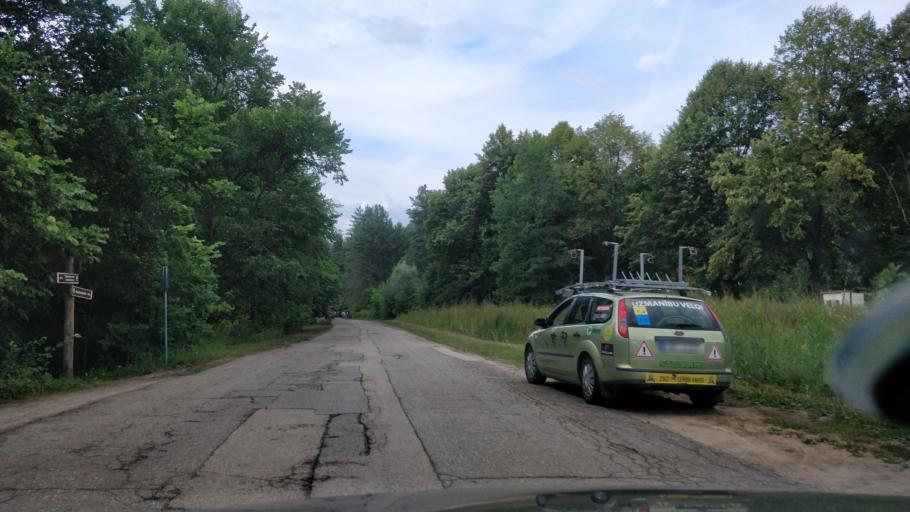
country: LV
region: Sigulda
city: Sigulda
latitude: 57.1562
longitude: 24.8365
